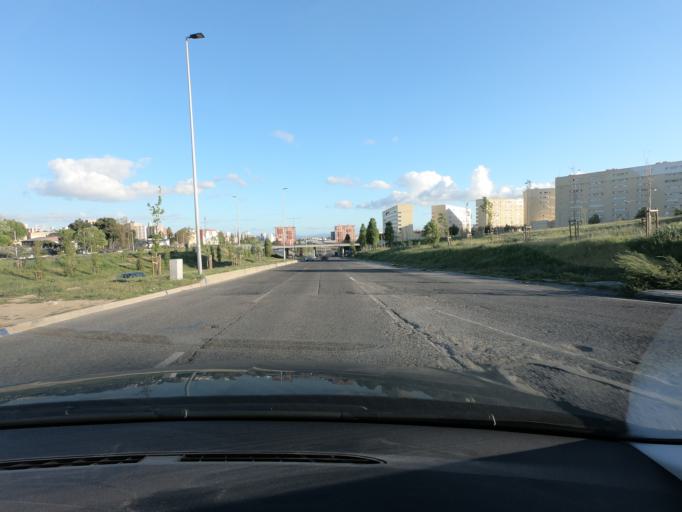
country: PT
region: Lisbon
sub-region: Loures
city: Moscavide
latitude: 38.7576
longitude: -9.1200
